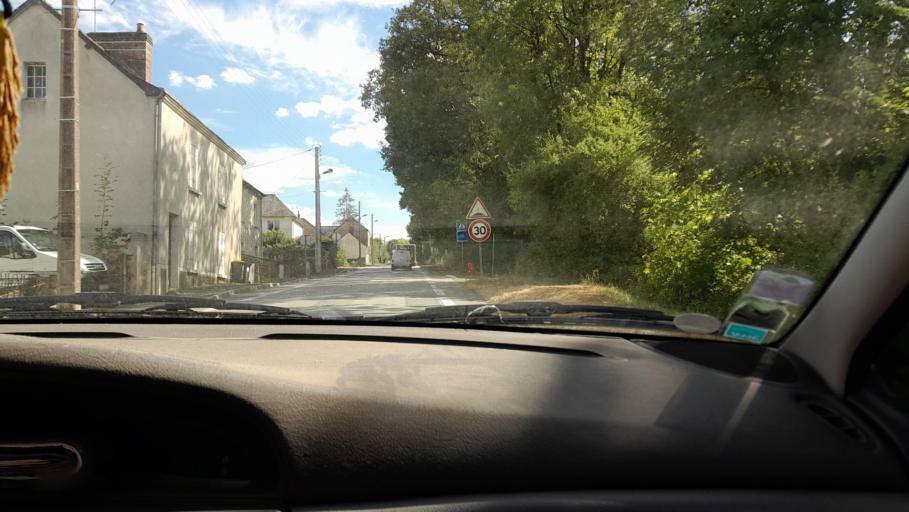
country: FR
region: Pays de la Loire
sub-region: Departement de la Mayenne
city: Saint-Berthevin
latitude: 48.0684
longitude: -0.8382
